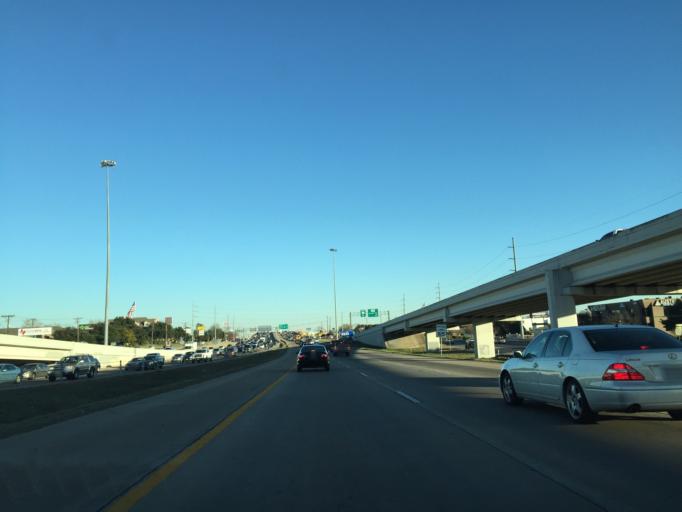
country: US
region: Texas
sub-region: Williamson County
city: Jollyville
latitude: 30.3769
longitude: -97.7337
